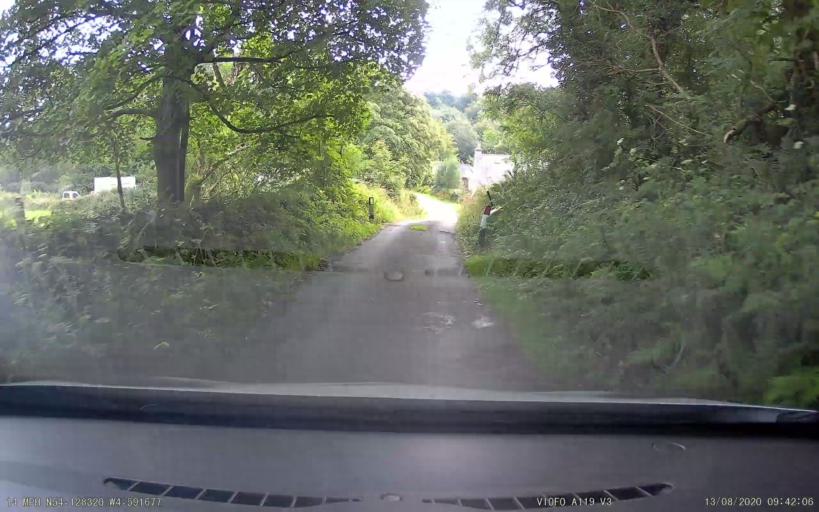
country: IM
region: Castletown
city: Castletown
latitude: 54.1283
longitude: -4.5917
